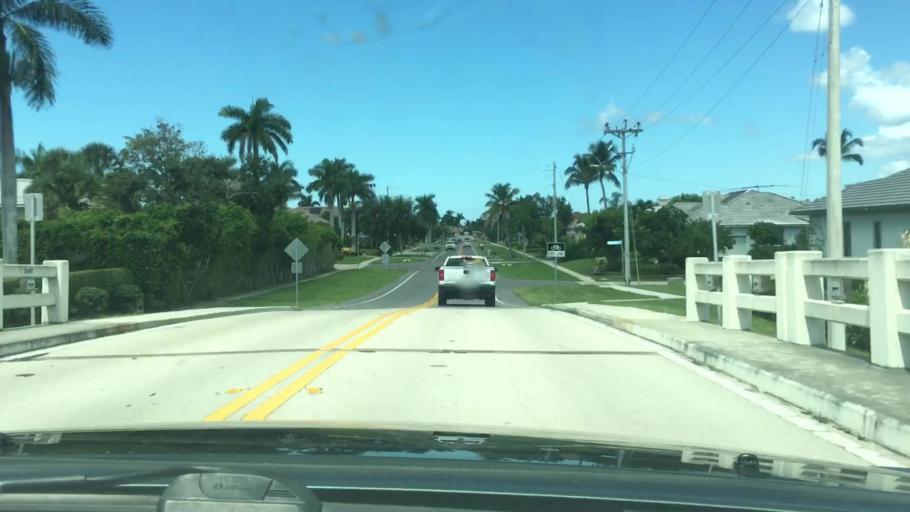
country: US
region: Florida
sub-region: Collier County
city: Marco
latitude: 25.9507
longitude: -81.7376
